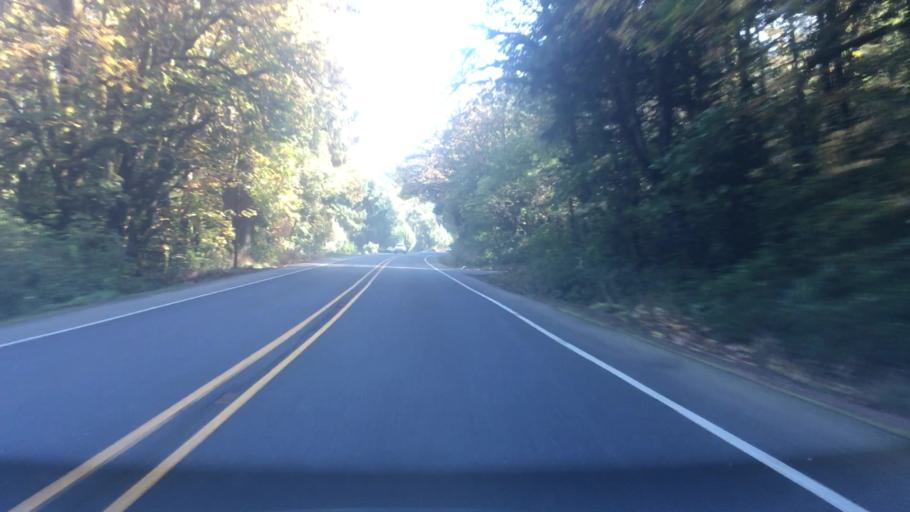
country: US
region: Oregon
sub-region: Lincoln County
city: Rose Lodge
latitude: 45.0064
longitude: -123.9170
